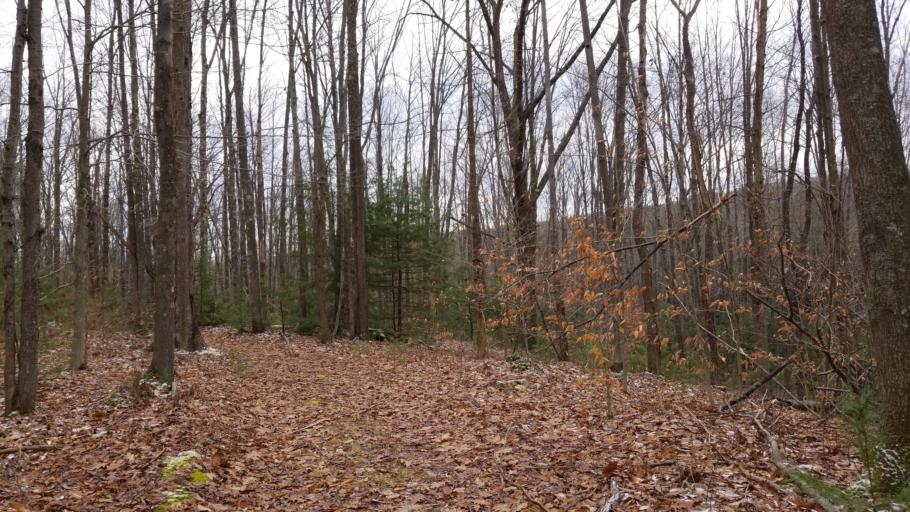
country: US
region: Pennsylvania
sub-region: Clearfield County
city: Clearfield
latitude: 41.1895
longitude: -78.5117
